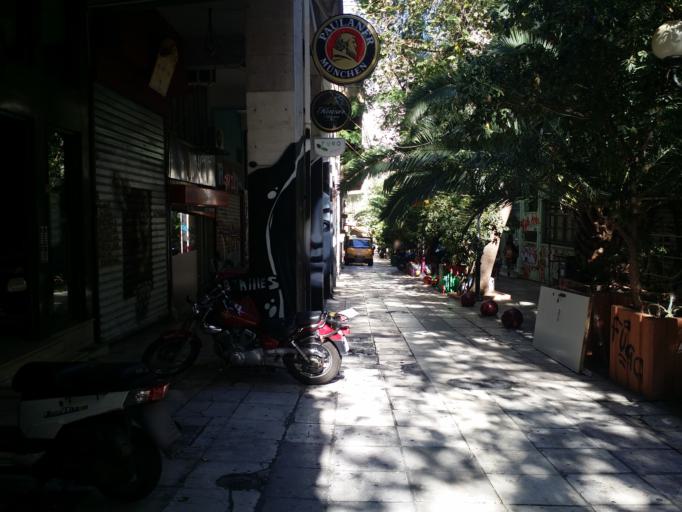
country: GR
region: Attica
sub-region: Nomarchia Athinas
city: Kipseli
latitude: 37.9856
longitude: 23.7331
